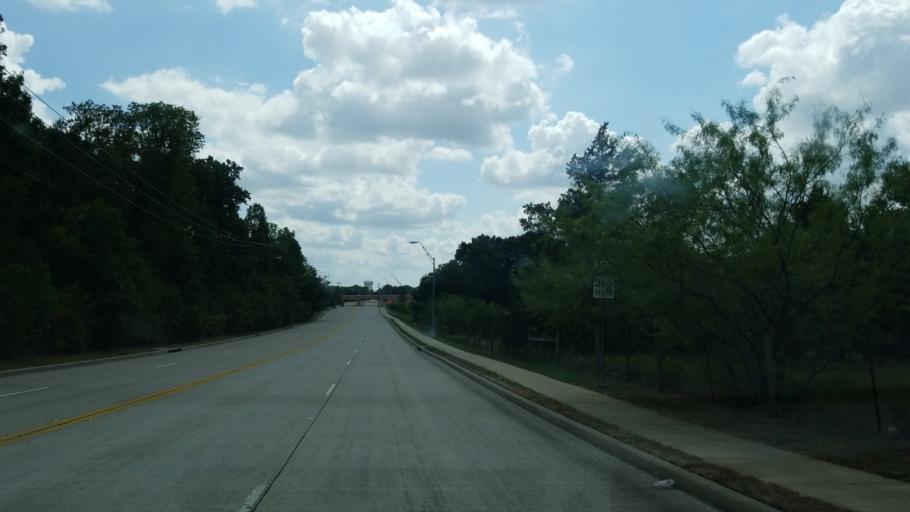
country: US
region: Texas
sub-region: Tarrant County
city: Grapevine
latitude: 32.8973
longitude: -97.0822
